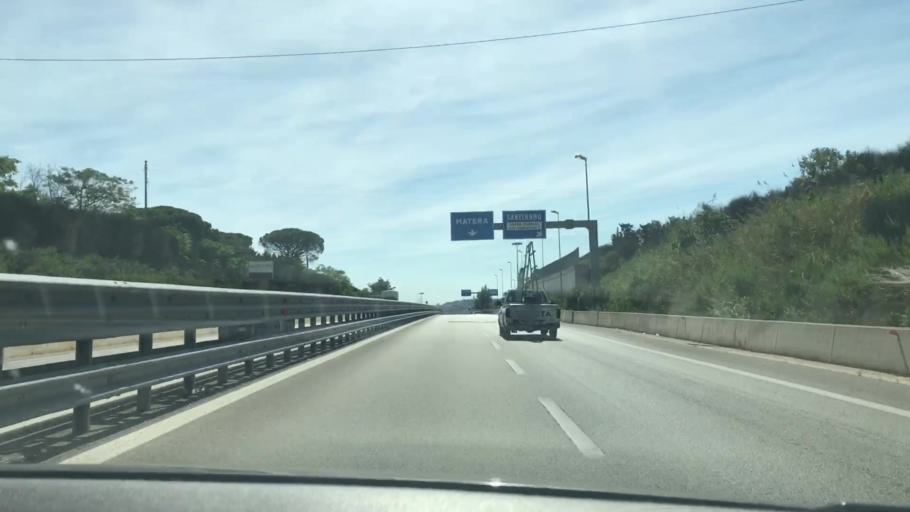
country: IT
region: Basilicate
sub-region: Provincia di Matera
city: Matera
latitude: 40.7042
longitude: 16.5846
